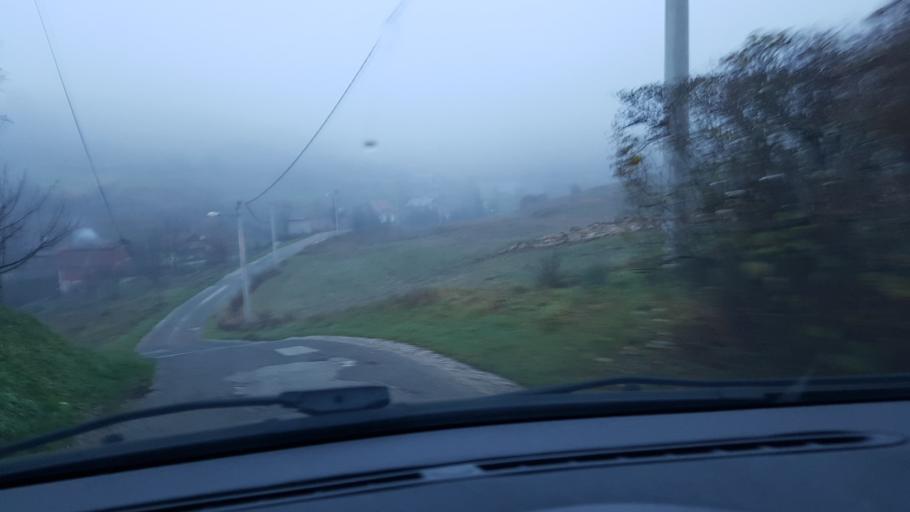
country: HR
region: Krapinsko-Zagorska
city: Pregrada
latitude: 46.1936
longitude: 15.7419
